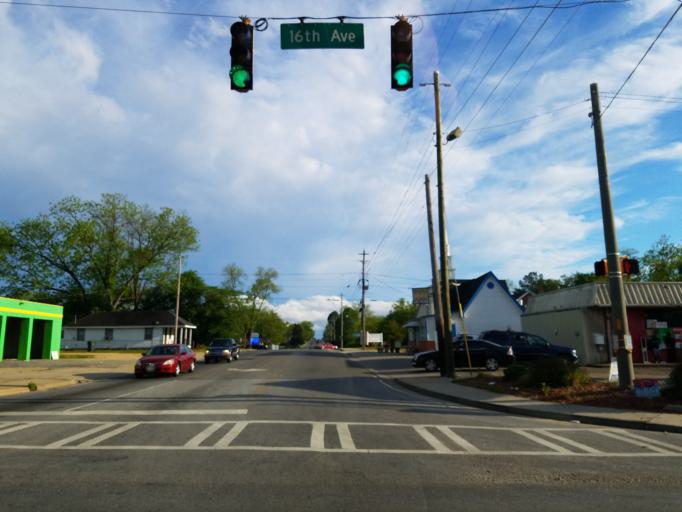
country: US
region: Georgia
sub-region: Crisp County
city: Cordele
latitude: 31.9635
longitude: -83.7880
